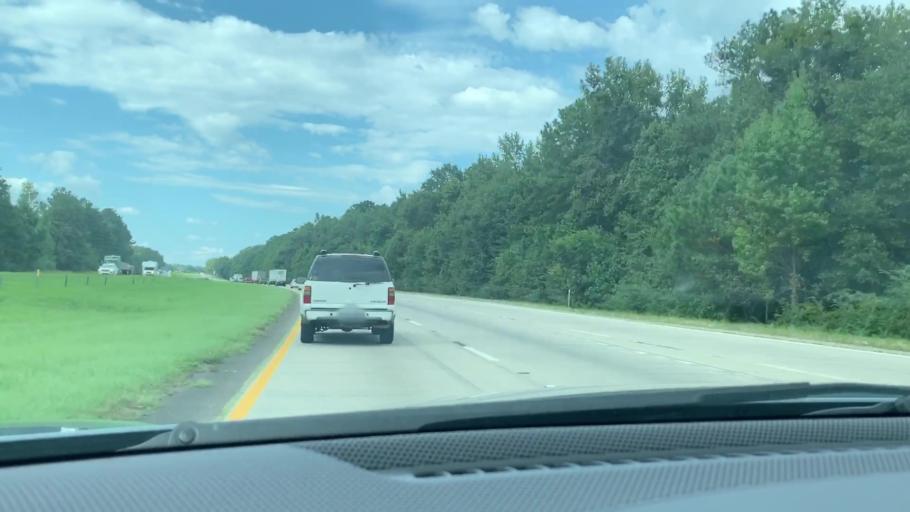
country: US
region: South Carolina
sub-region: Hampton County
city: Yemassee
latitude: 32.6357
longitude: -80.8814
